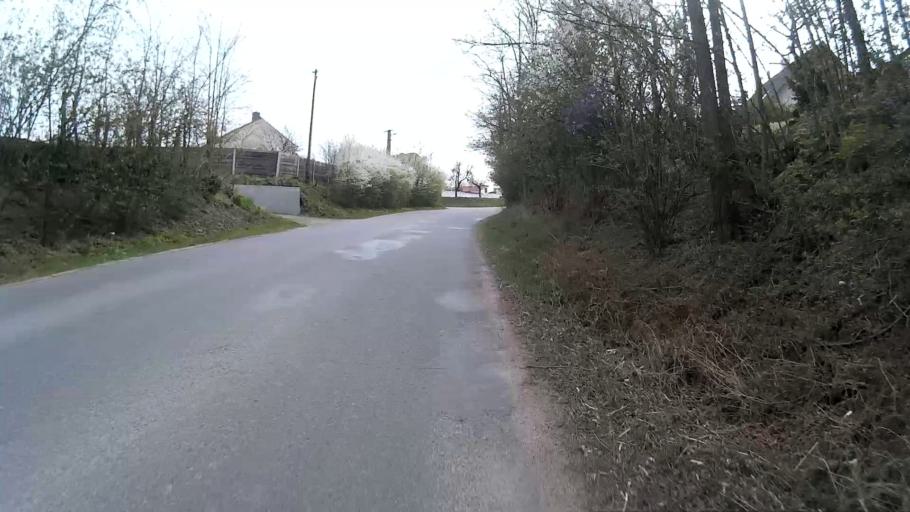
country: CZ
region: South Moravian
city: Orechov
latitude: 49.0772
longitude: 16.5443
